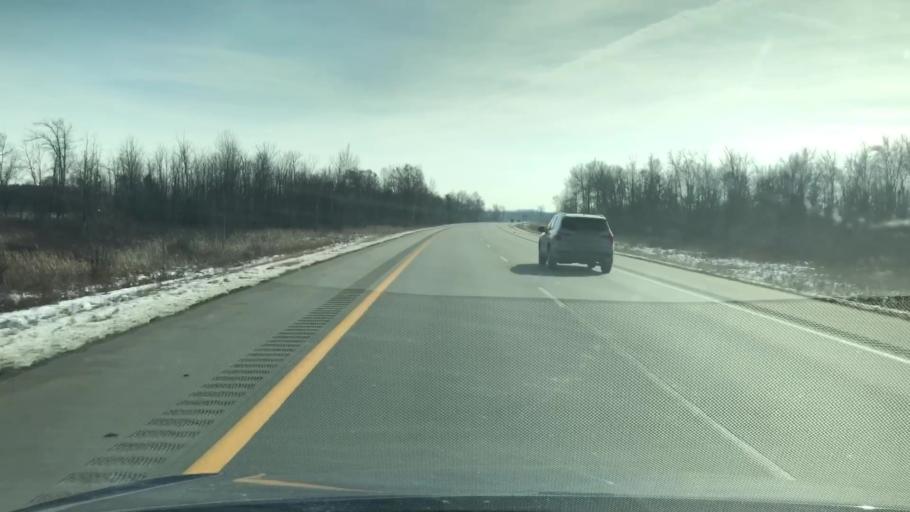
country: US
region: Michigan
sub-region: Ogemaw County
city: Skidway Lake
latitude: 44.0964
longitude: -84.1102
